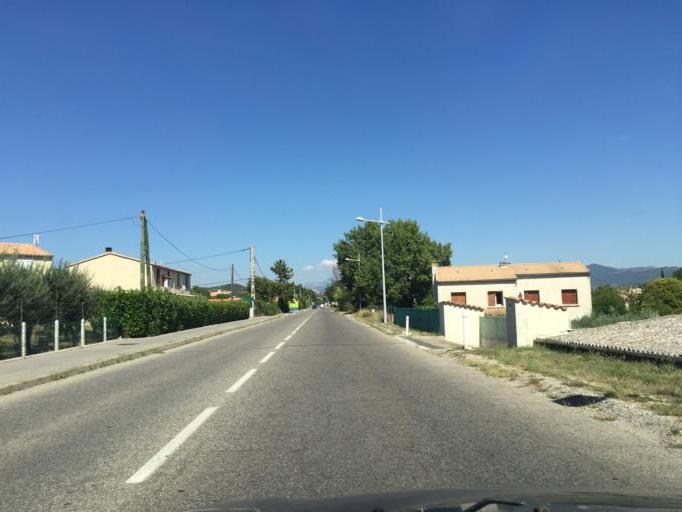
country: FR
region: Provence-Alpes-Cote d'Azur
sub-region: Departement des Alpes-de-Haute-Provence
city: Peyruis
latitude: 44.0306
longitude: 5.9427
